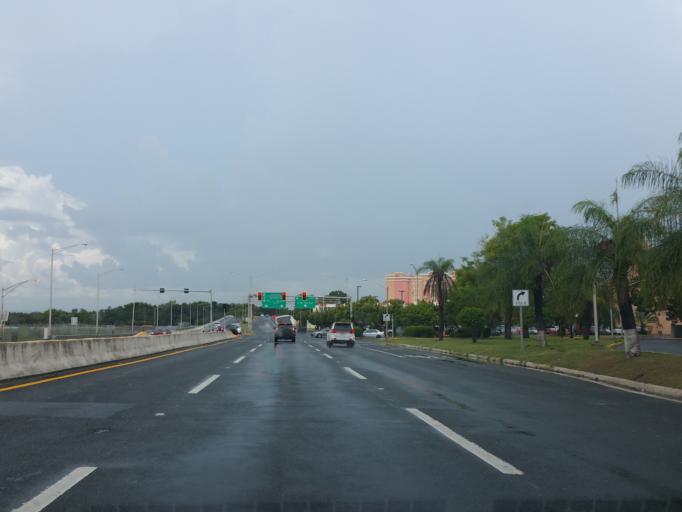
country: PR
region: Carolina
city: Carolina
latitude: 18.4401
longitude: -66.0182
